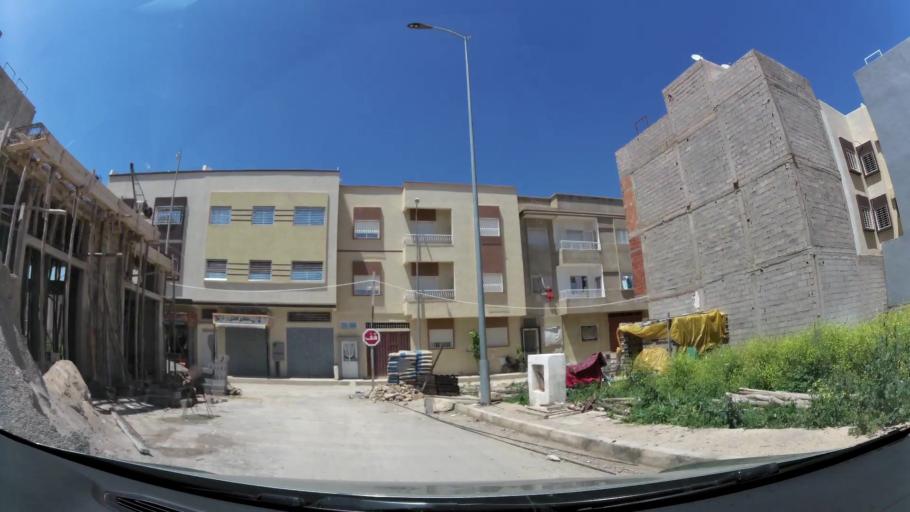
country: MA
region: Fes-Boulemane
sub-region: Fes
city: Fes
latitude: 34.0306
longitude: -5.0527
